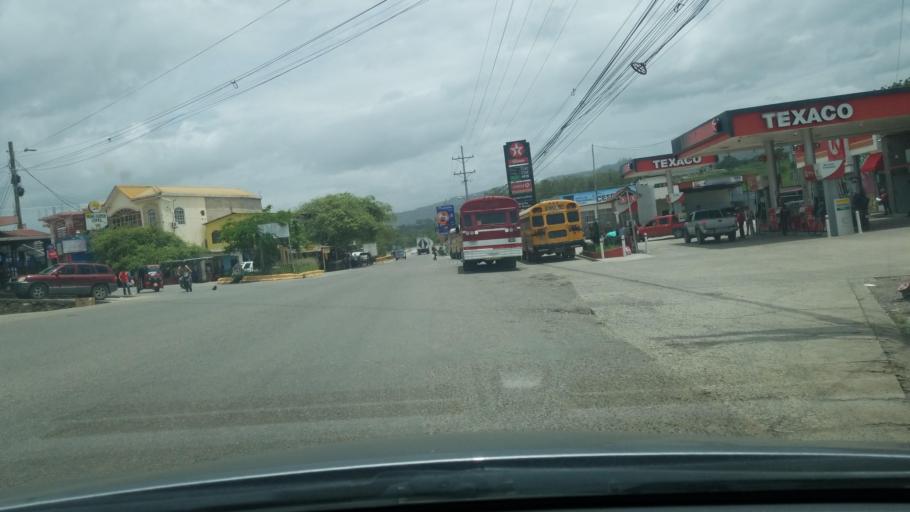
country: HN
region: Copan
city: Cucuyagua
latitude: 14.6517
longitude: -88.8763
